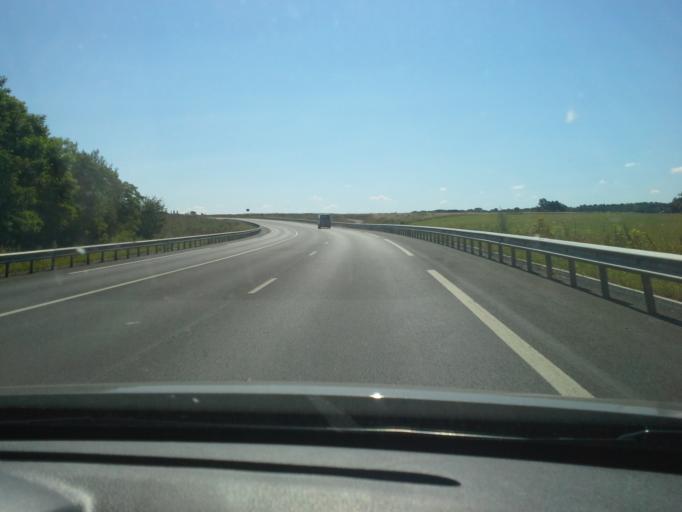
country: FR
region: Centre
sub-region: Departement du Loir-et-Cher
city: Naveil
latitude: 47.7728
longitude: 1.0359
